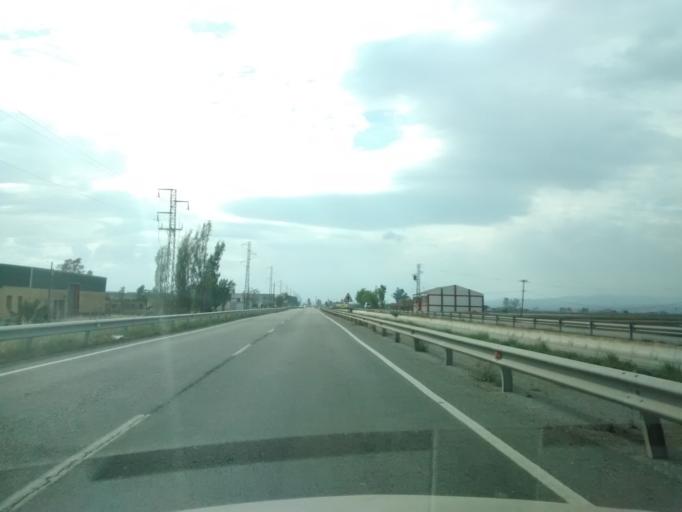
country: ES
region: Catalonia
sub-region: Provincia de Tarragona
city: Deltebre
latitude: 40.7259
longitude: 0.7128
